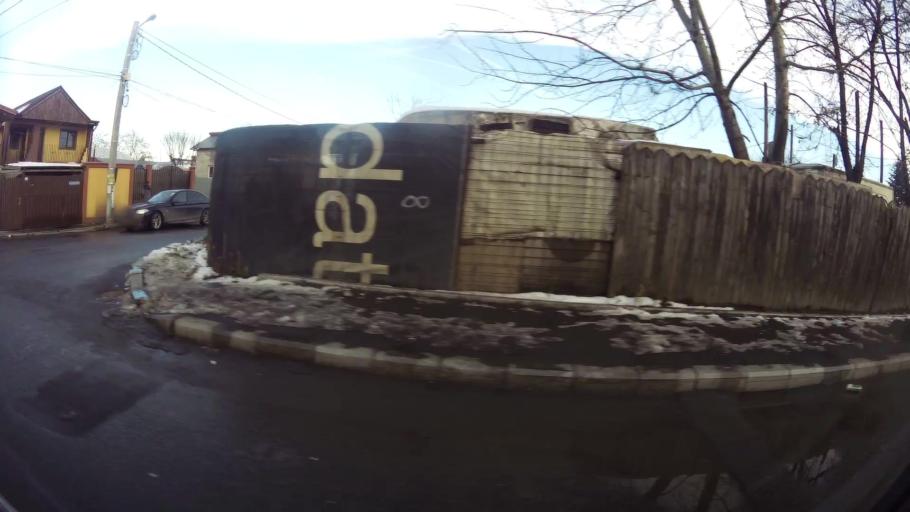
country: RO
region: Bucuresti
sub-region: Municipiul Bucuresti
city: Bucuresti
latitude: 44.3913
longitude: 26.0696
